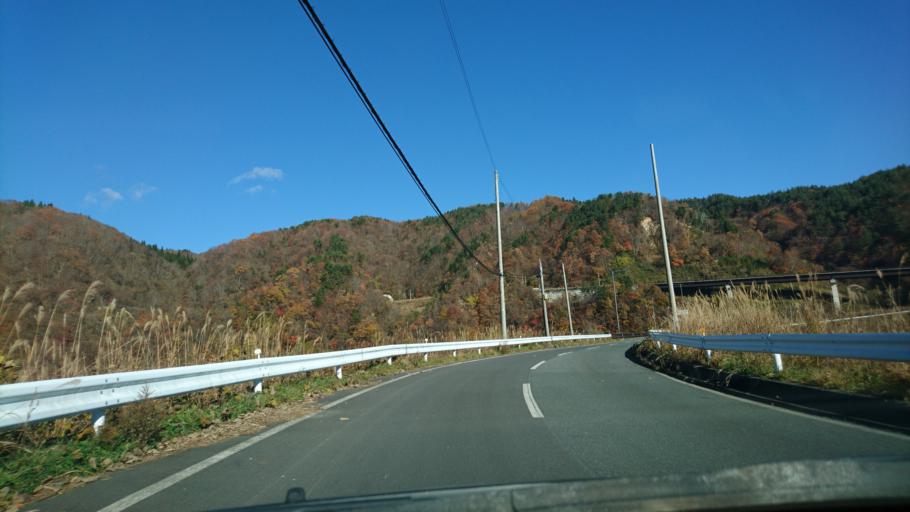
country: JP
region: Iwate
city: Mizusawa
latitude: 39.1211
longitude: 140.9334
